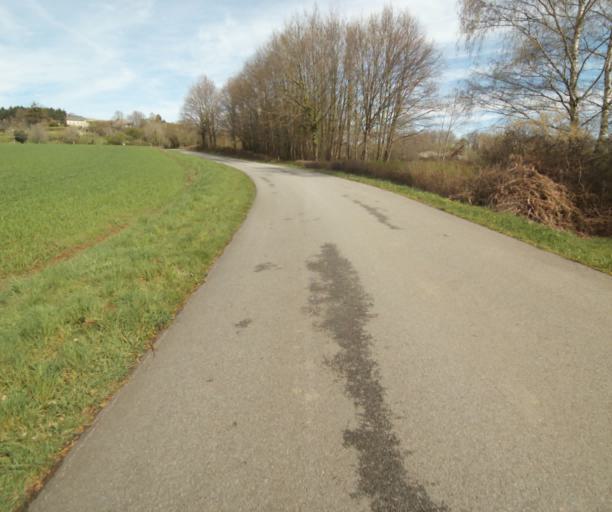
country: FR
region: Limousin
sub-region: Departement de la Correze
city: Laguenne
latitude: 45.2666
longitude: 1.8167
